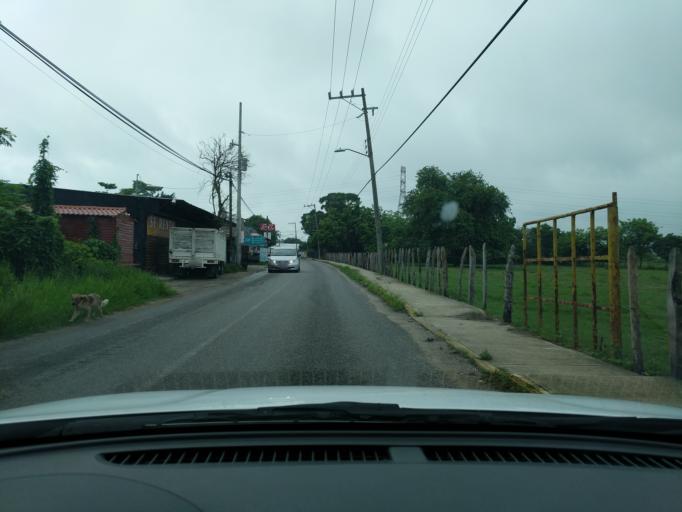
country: MX
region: Tabasco
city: Villahermosa
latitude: 17.9516
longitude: -92.9649
